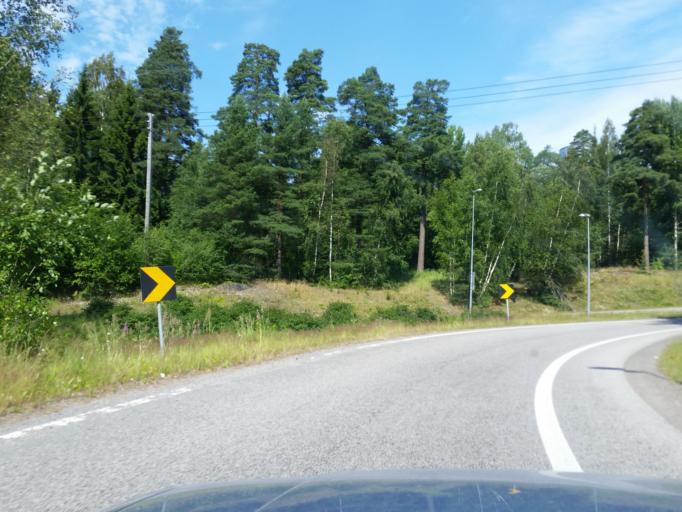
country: FI
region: Uusimaa
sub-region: Helsinki
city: Espoo
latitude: 60.1542
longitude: 24.6615
